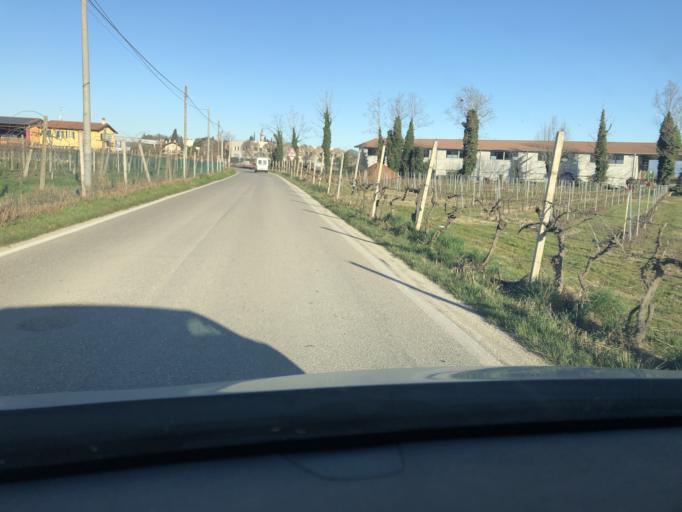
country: IT
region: Veneto
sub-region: Provincia di Verona
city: Sommacampagna
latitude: 45.4000
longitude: 10.8534
